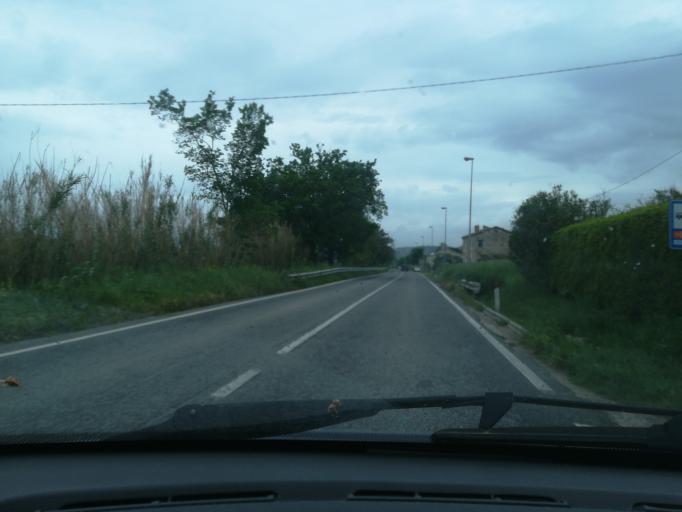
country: IT
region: The Marches
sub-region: Provincia di Macerata
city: Tolentino
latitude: 43.2678
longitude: 13.2623
